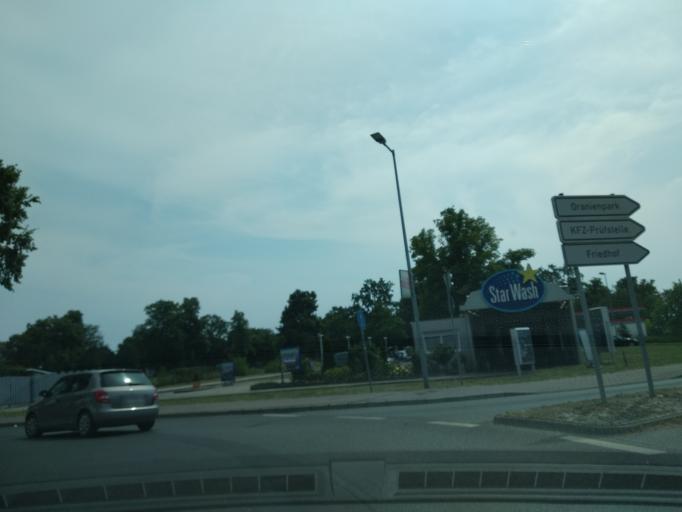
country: DE
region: Brandenburg
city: Oranienburg
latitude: 52.7509
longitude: 13.2265
